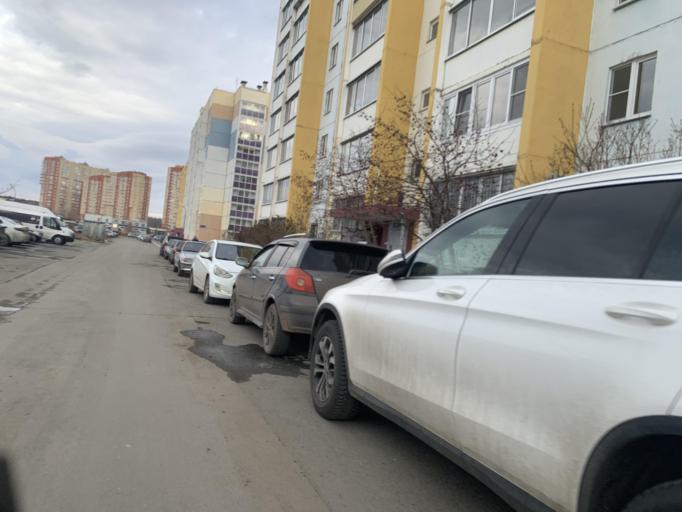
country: RU
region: Chelyabinsk
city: Roshchino
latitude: 55.1913
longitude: 61.2741
